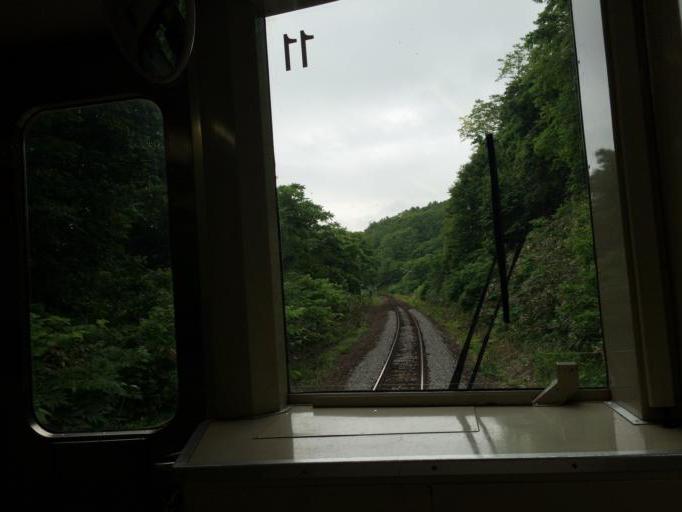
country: JP
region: Hokkaido
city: Otaru
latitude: 43.2096
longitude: 140.9378
